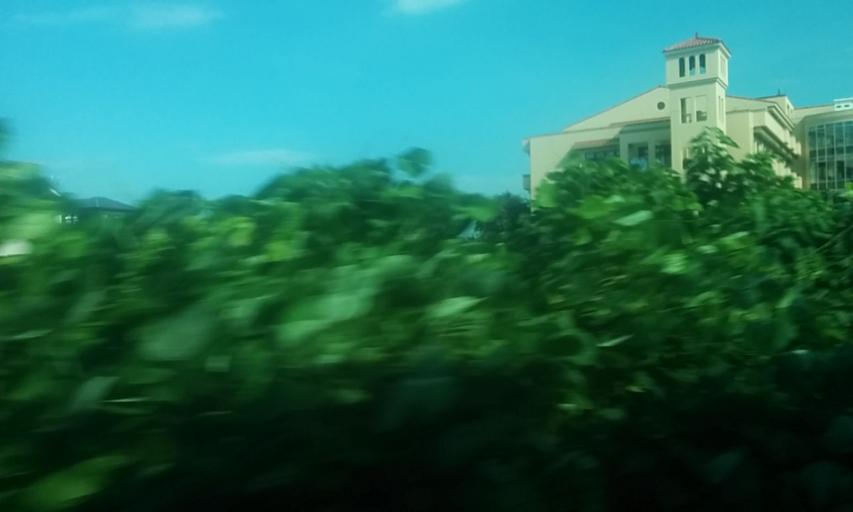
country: JP
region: Saitama
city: Shiraoka
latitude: 36.0054
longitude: 139.6647
